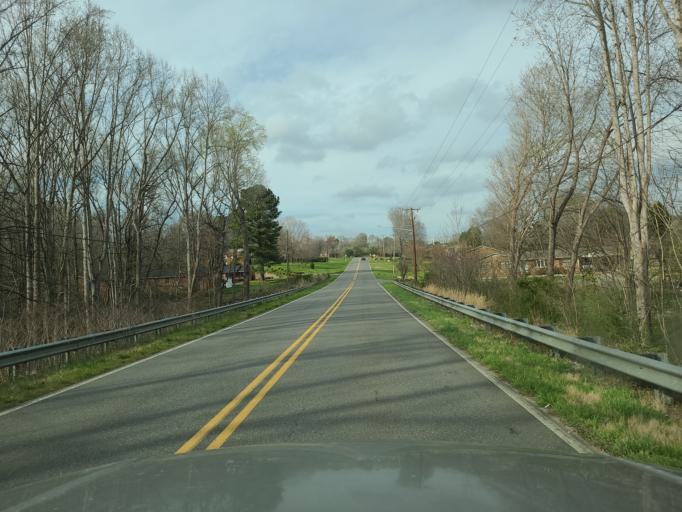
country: US
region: North Carolina
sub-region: Cleveland County
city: Shelby
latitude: 35.2716
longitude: -81.5687
